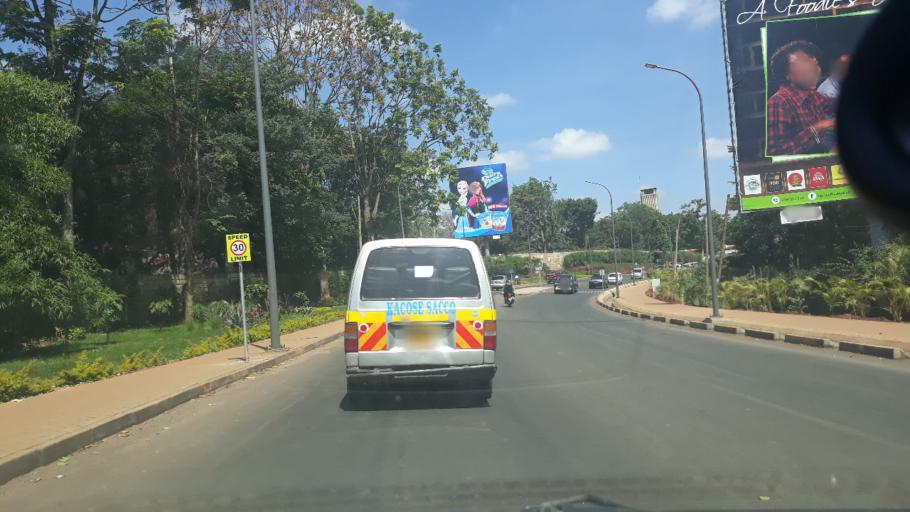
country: KE
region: Nairobi Area
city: Nairobi
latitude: -1.2334
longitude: 36.8032
